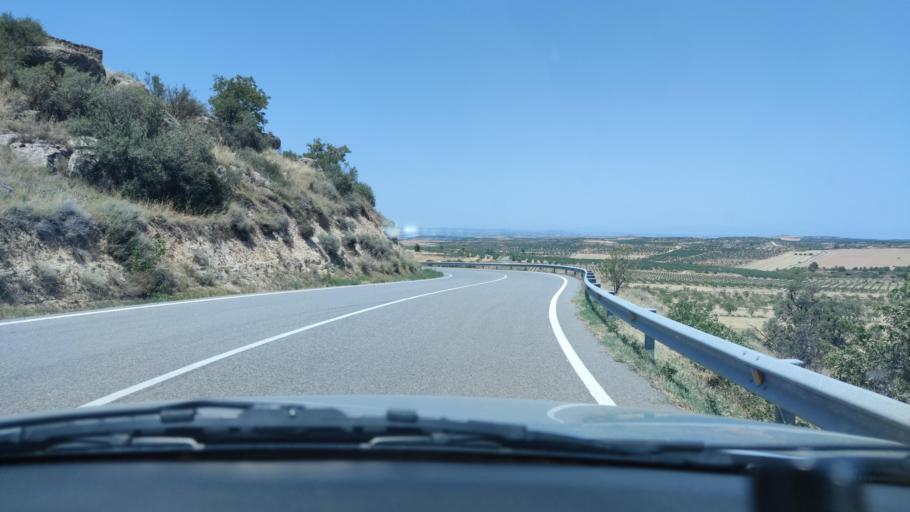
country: ES
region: Catalonia
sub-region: Provincia de Lleida
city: el Cogul
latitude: 41.4353
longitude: 0.6482
